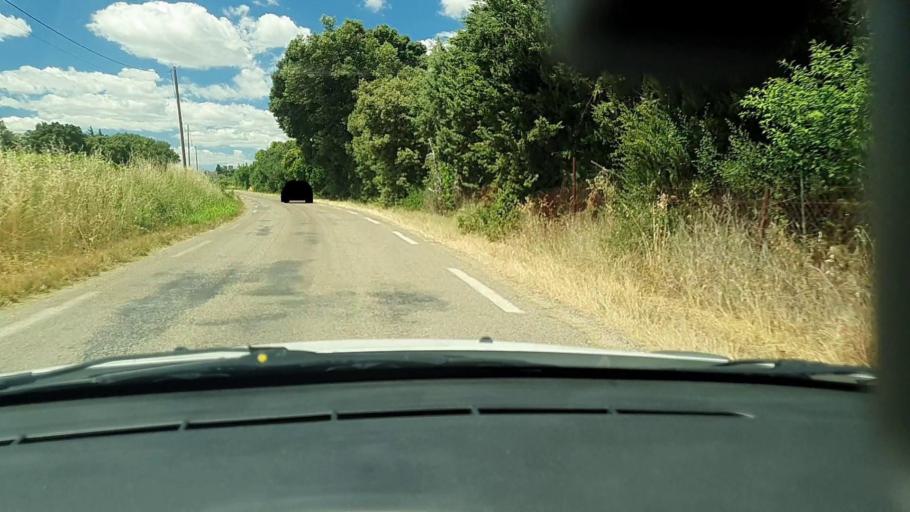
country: FR
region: Languedoc-Roussillon
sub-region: Departement du Gard
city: Poulx
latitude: 43.9556
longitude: 4.4398
